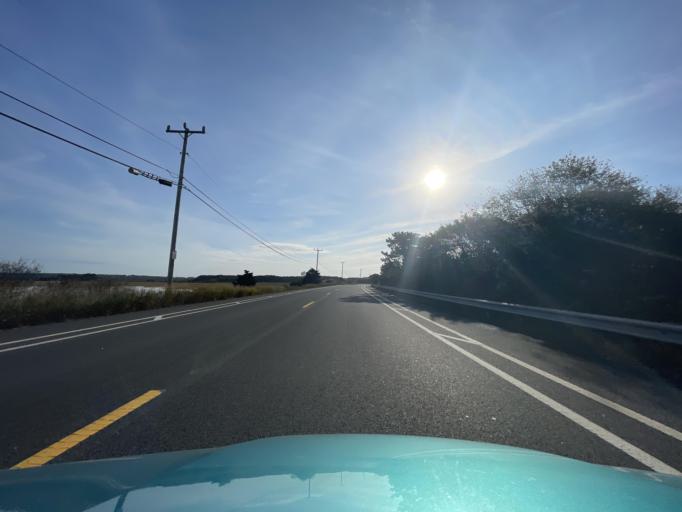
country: US
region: Massachusetts
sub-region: Bristol County
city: Head of Westport
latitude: 41.5094
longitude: -71.0567
